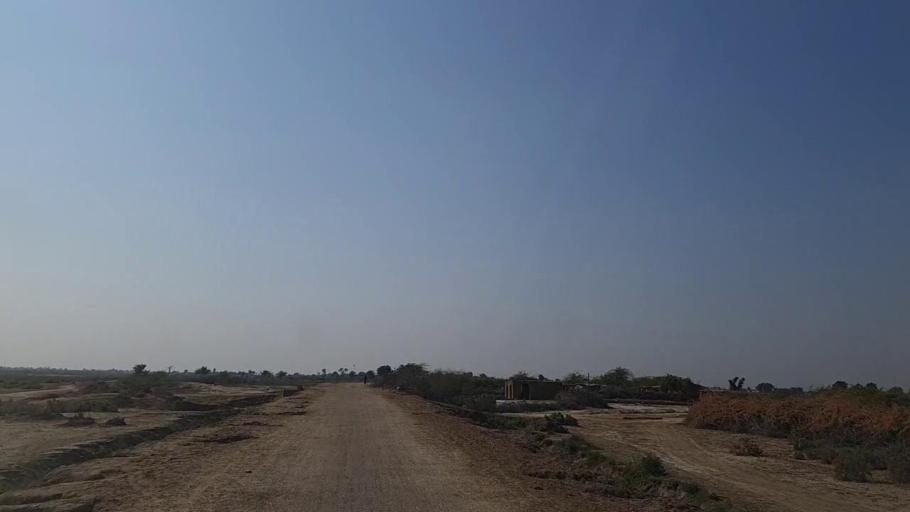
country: PK
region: Sindh
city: Naukot
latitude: 24.9021
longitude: 69.4277
